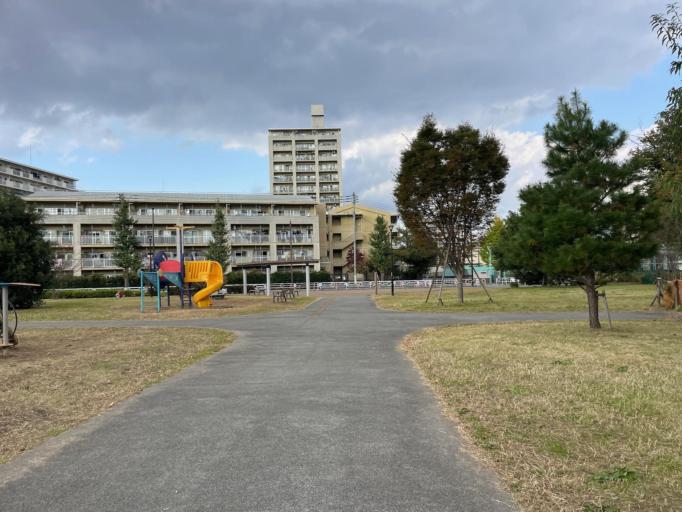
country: JP
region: Tokyo
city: Hino
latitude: 35.7186
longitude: 139.3892
